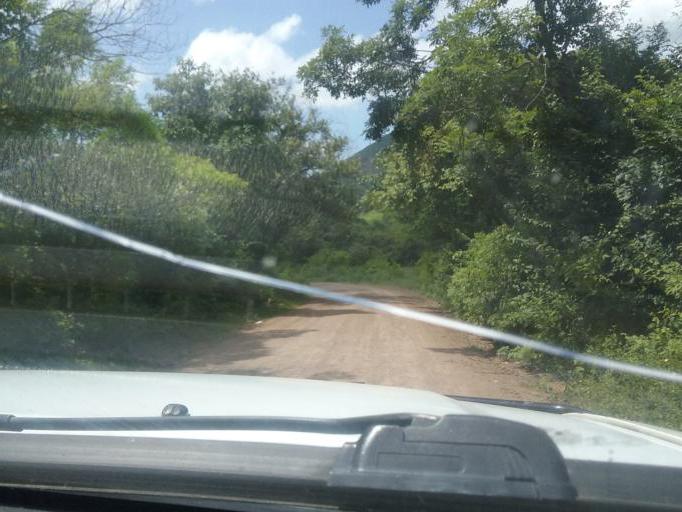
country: NI
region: Matagalpa
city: Terrabona
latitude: 12.7194
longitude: -85.9648
